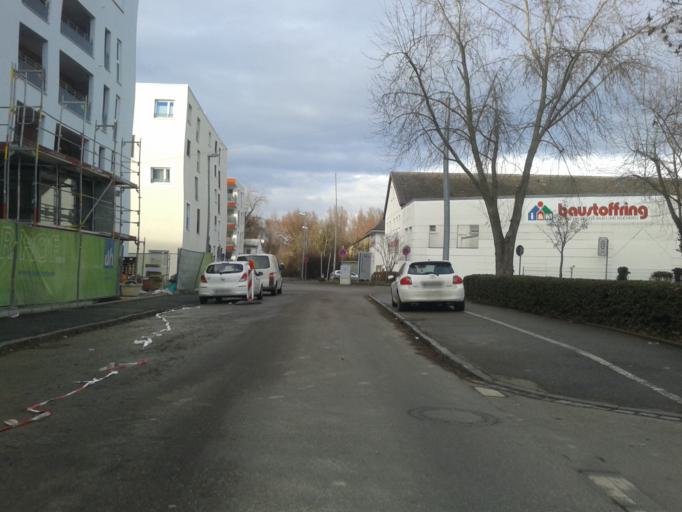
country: DE
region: Baden-Wuerttemberg
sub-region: Tuebingen Region
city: Ulm
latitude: 48.3970
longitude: 9.9746
